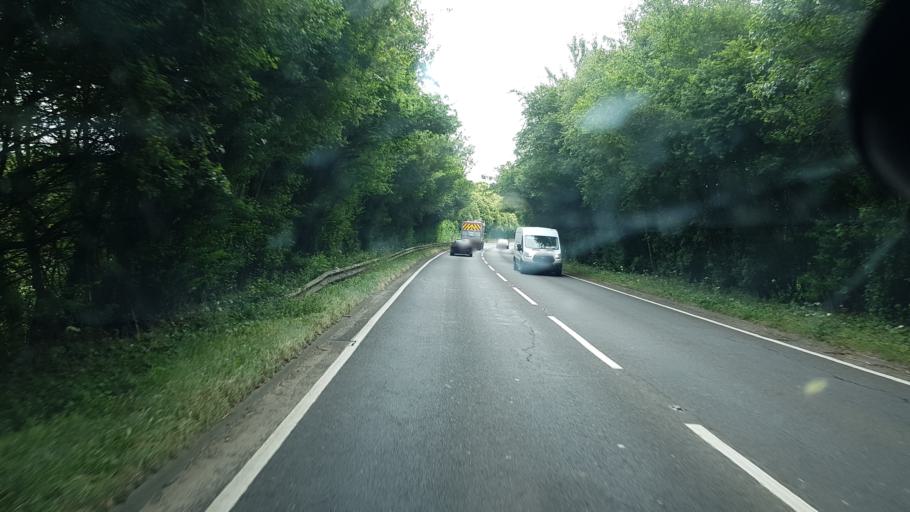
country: GB
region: England
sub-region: Surrey
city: Godstone
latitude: 51.2438
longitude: -0.0487
